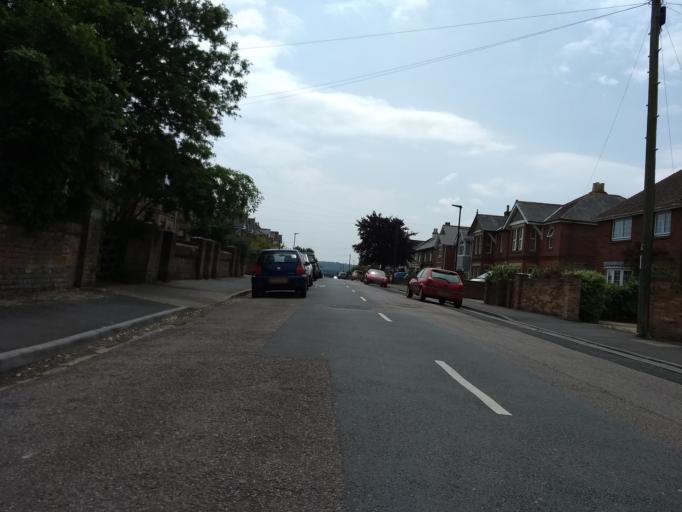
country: GB
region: England
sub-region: Isle of Wight
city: Ryde
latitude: 50.7192
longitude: -1.1493
